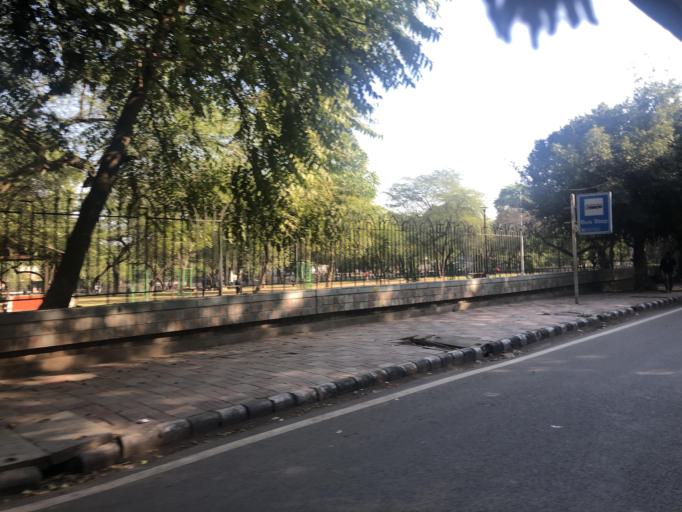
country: IN
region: NCT
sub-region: Central Delhi
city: Karol Bagh
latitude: 28.5554
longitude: 77.1645
